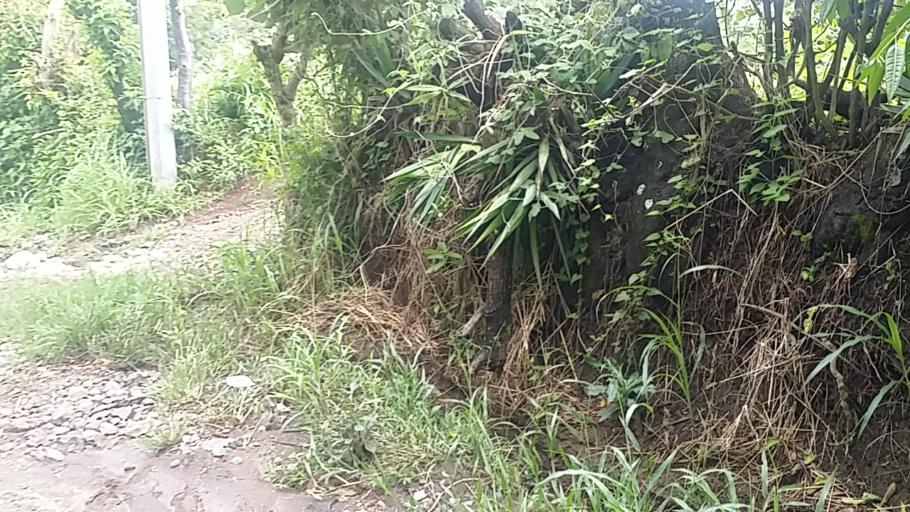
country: GT
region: Santa Rosa
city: Pueblo Nuevo Vinas
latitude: 14.3269
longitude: -90.5163
